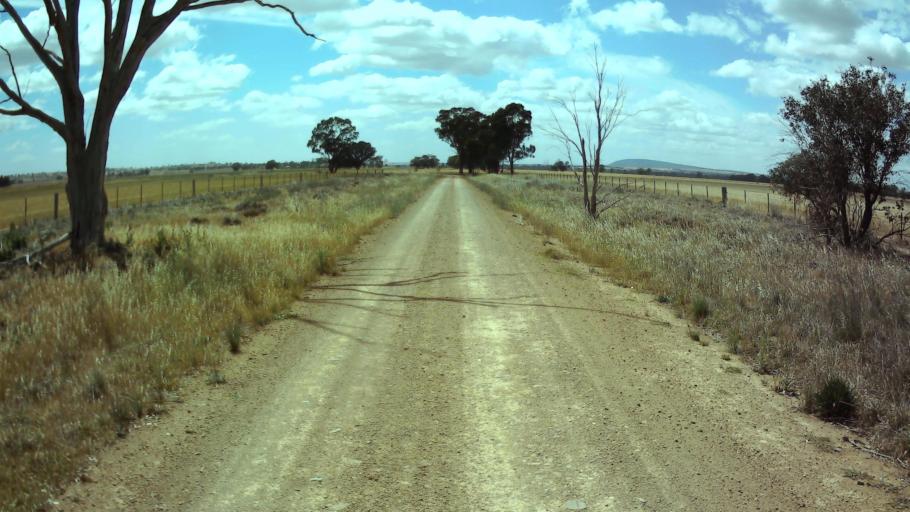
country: AU
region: New South Wales
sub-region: Weddin
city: Grenfell
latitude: -33.9963
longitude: 148.2867
